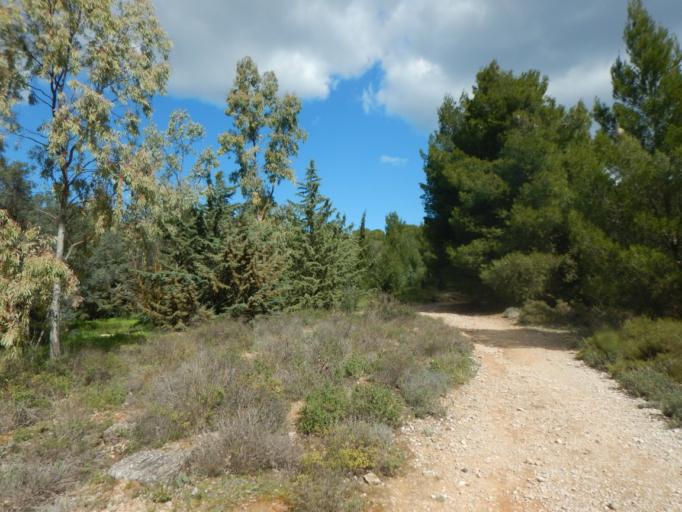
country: GR
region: Attica
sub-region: Nomarchia Athinas
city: Kifisia
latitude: 38.0609
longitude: 23.8137
